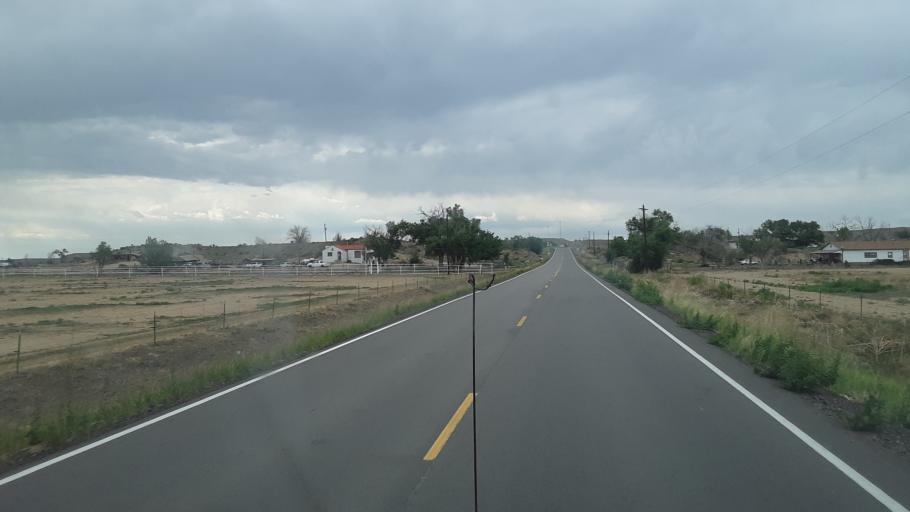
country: US
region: Colorado
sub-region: Otero County
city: Fowler
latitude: 38.1509
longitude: -104.0231
